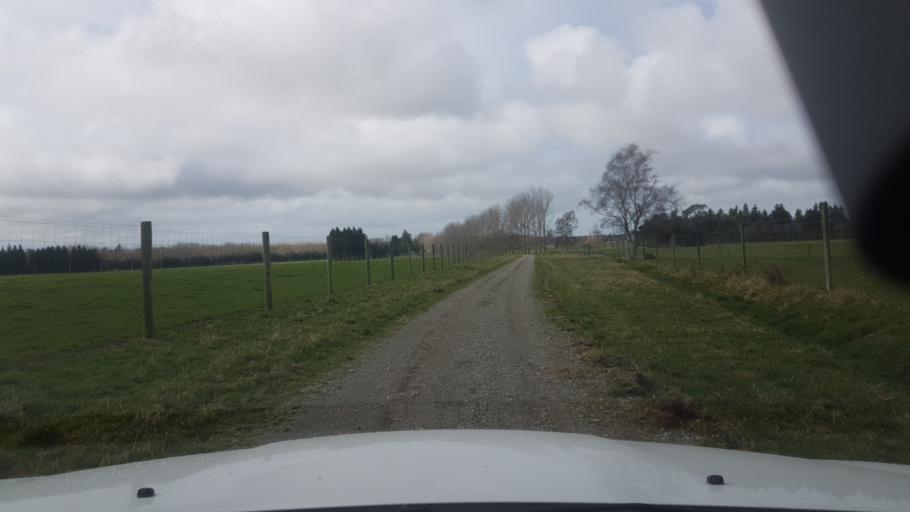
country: NZ
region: Canterbury
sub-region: Timaru District
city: Pleasant Point
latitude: -44.0104
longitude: 171.2028
